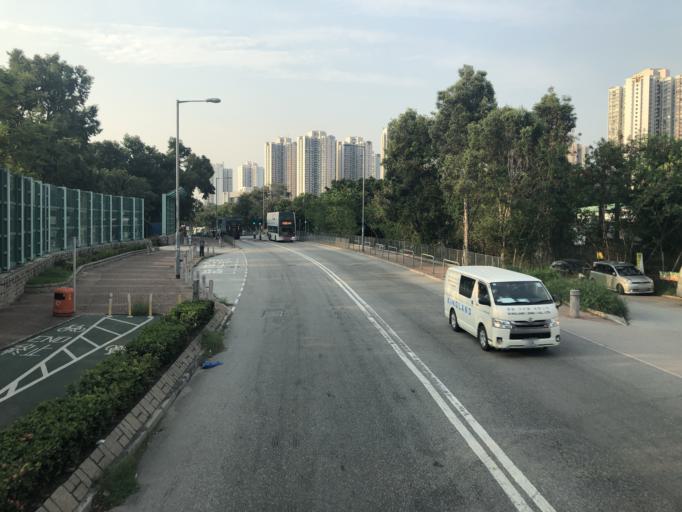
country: HK
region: Yuen Long
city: Yuen Long Kau Hui
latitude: 22.4508
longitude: 113.9949
